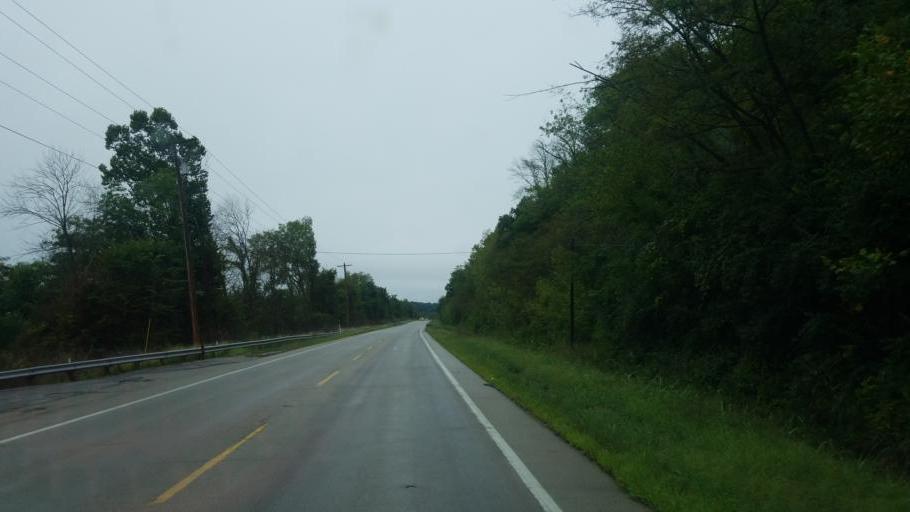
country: US
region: Kentucky
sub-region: Mason County
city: Maysville
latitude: 38.6498
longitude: -83.7415
